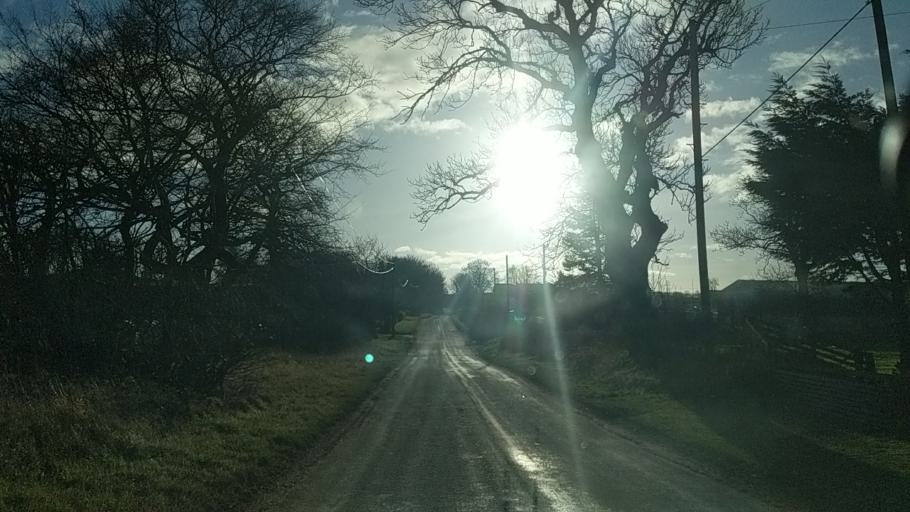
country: GB
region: Scotland
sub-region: West Lothian
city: Linlithgow
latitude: 55.9810
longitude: -3.5338
